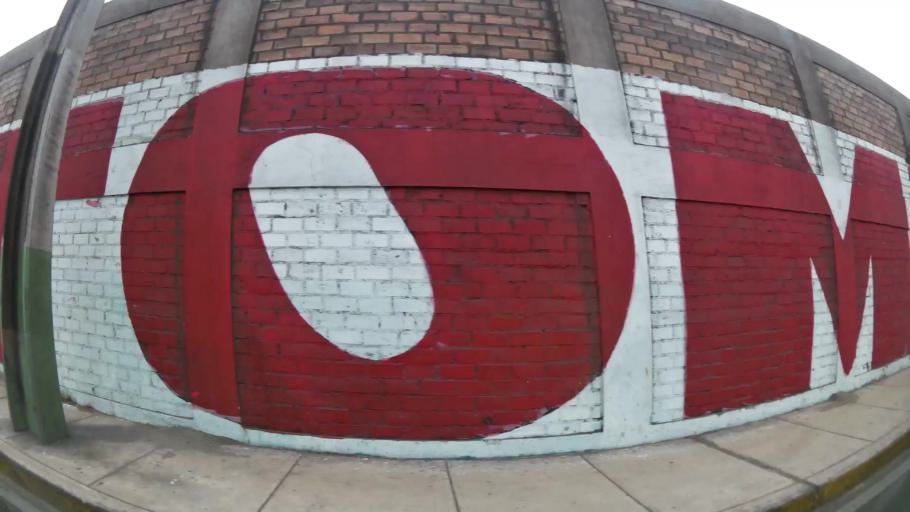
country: PE
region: Callao
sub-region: Callao
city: Callao
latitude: -12.0479
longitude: -77.1354
